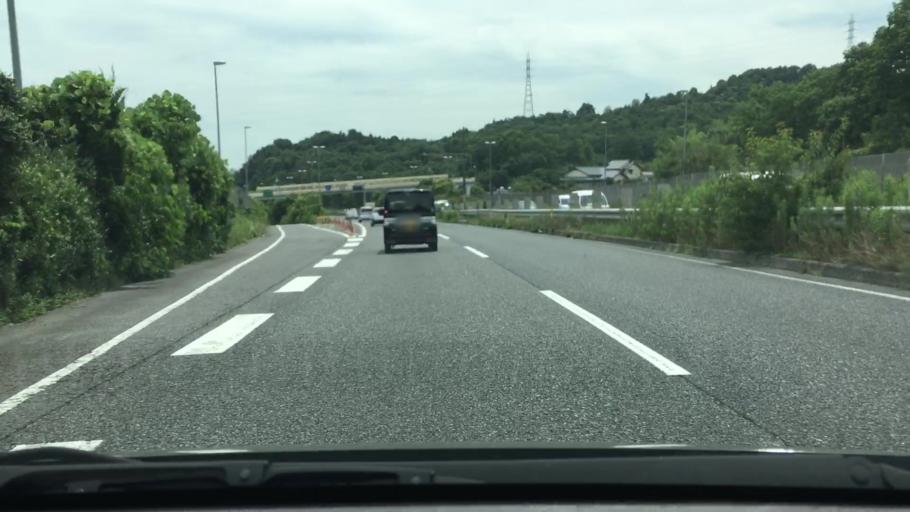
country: JP
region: Hiroshima
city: Hatsukaichi
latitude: 34.3683
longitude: 132.3327
